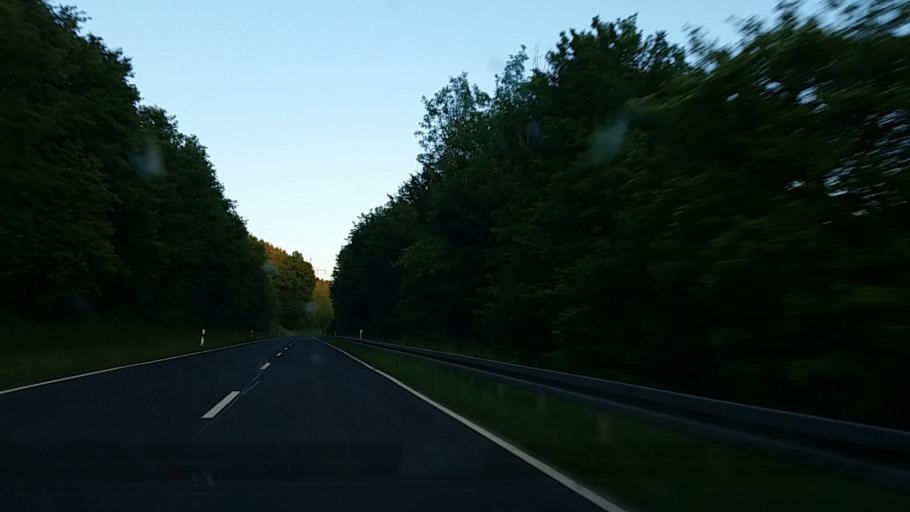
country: DE
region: Bavaria
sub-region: Regierungsbezirk Unterfranken
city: Mittelsinn
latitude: 50.1798
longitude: 9.6338
